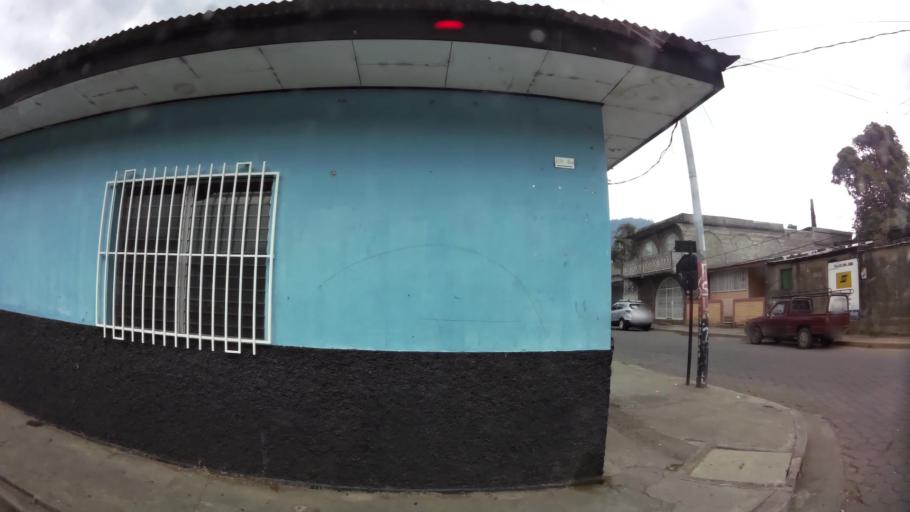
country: NI
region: Jinotega
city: Jinotega
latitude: 13.0916
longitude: -86.0046
